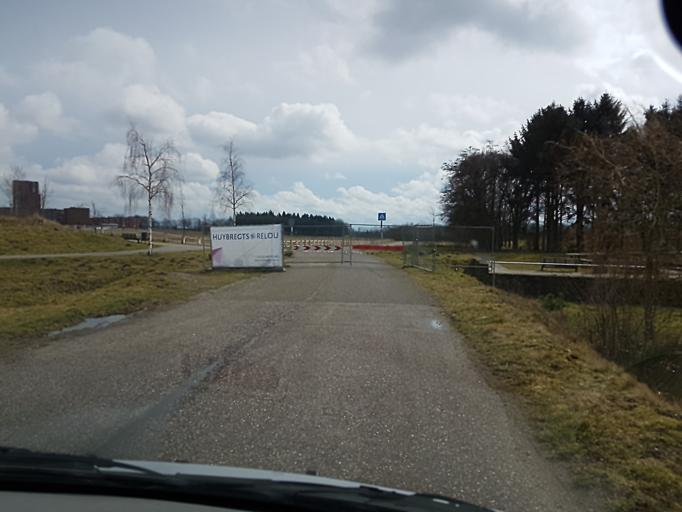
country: NL
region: North Brabant
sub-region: Gemeente Eindhoven
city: Meerhoven
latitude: 51.4445
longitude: 5.3997
